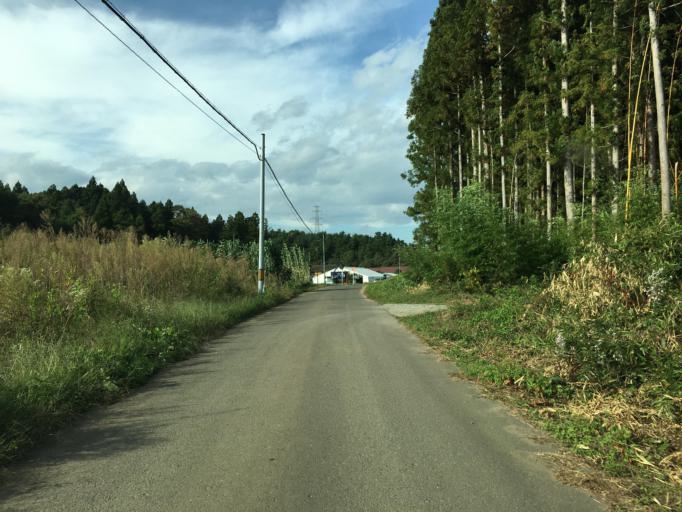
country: JP
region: Fukushima
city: Nihommatsu
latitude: 37.6266
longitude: 140.4131
